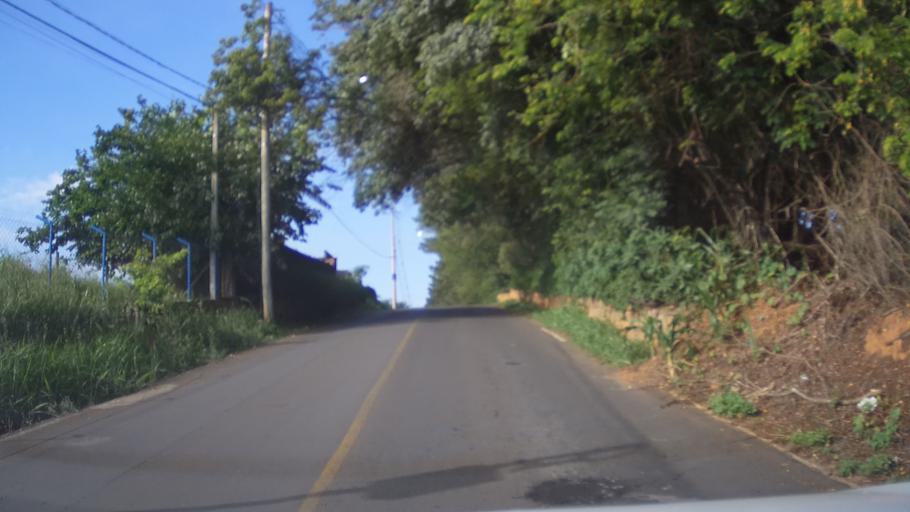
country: BR
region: Sao Paulo
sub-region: Itupeva
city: Itupeva
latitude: -23.2064
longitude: -47.0685
